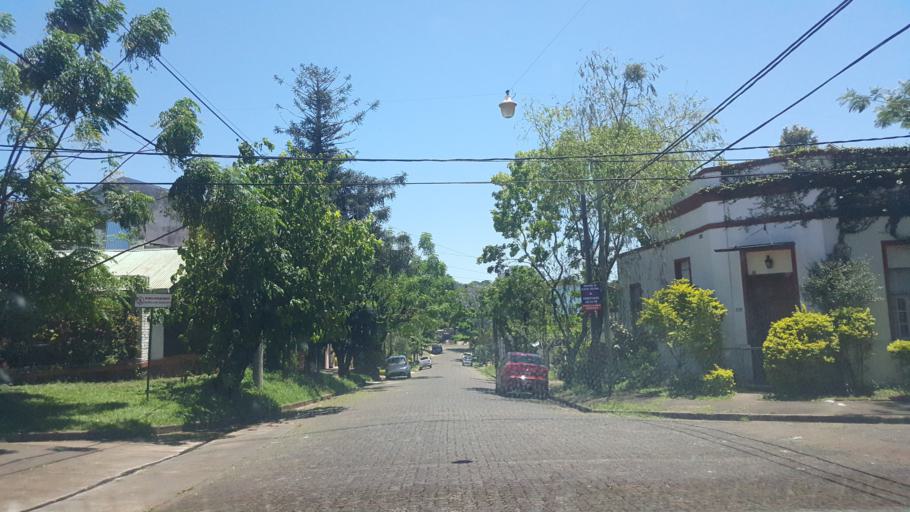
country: AR
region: Misiones
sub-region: Departamento de Capital
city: Posadas
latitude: -27.3627
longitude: -55.9026
